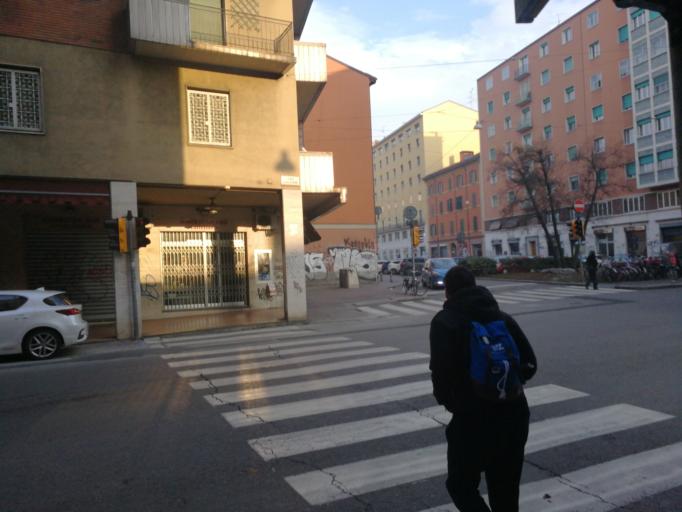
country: IT
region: Emilia-Romagna
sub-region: Provincia di Bologna
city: Bologna
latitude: 44.4987
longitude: 11.3355
